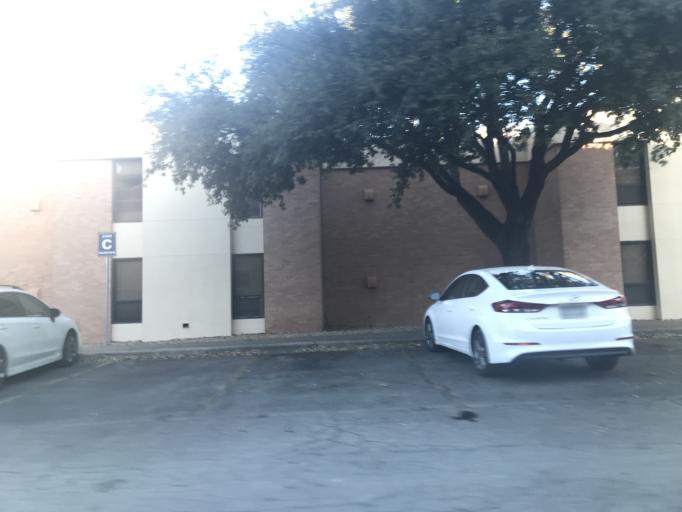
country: US
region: Texas
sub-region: Tom Green County
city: San Angelo
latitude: 31.4415
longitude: -100.4573
